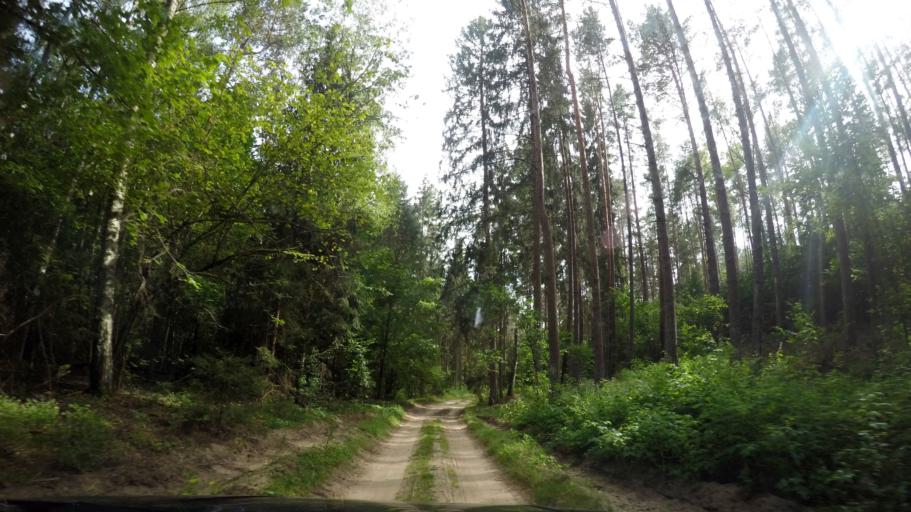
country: BY
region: Grodnenskaya
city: Skidal'
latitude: 53.8370
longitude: 24.1768
